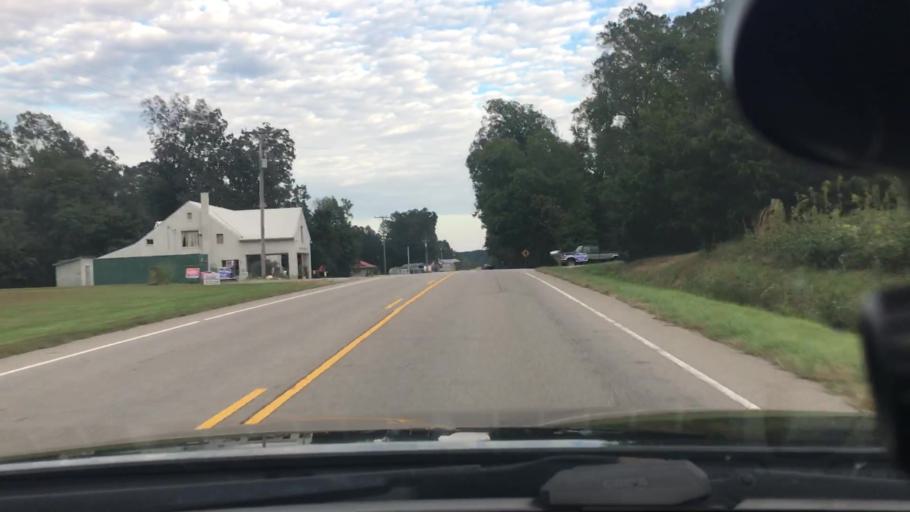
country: US
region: North Carolina
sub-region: Moore County
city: Carthage
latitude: 35.3863
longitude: -79.4973
